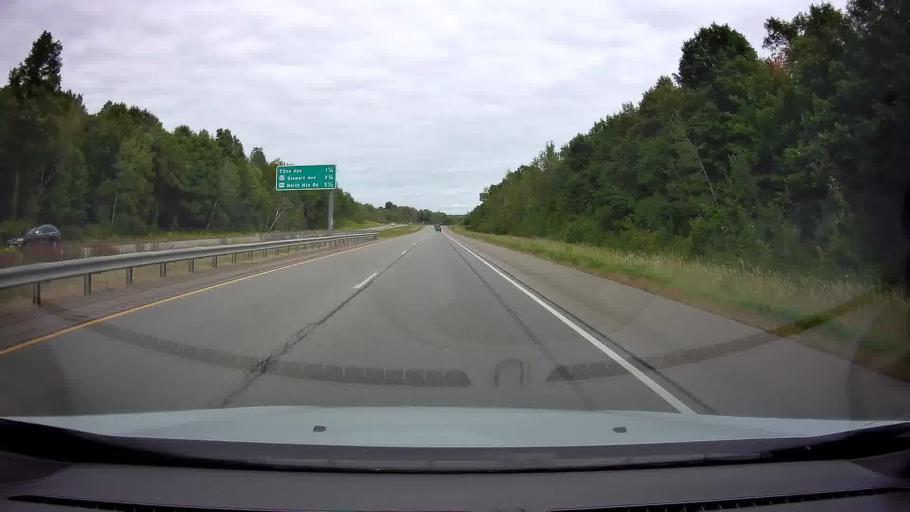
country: US
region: Wisconsin
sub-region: Marathon County
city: Marathon
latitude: 44.9463
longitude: -89.7556
